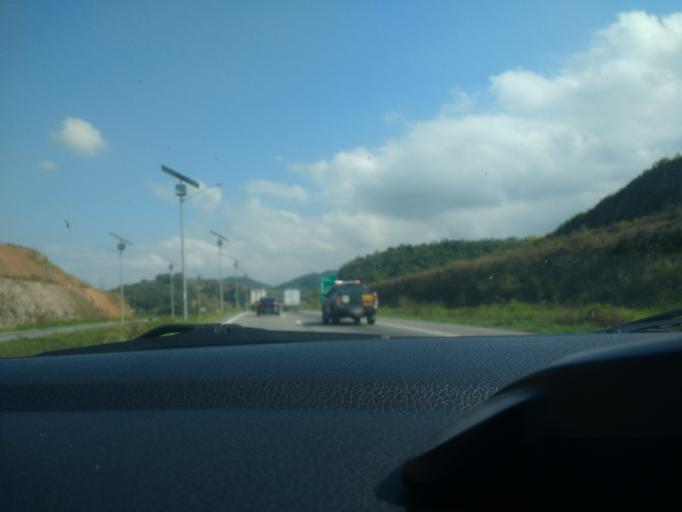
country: BR
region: Rio de Janeiro
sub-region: Nova Iguacu
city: Nova Iguacu
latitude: -22.6825
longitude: -43.4641
